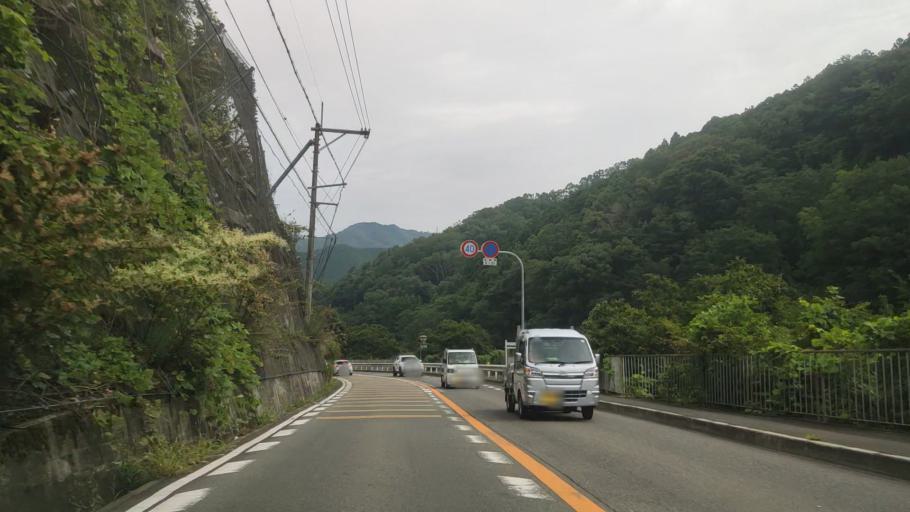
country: JP
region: Wakayama
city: Hashimoto
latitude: 34.3849
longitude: 135.6015
